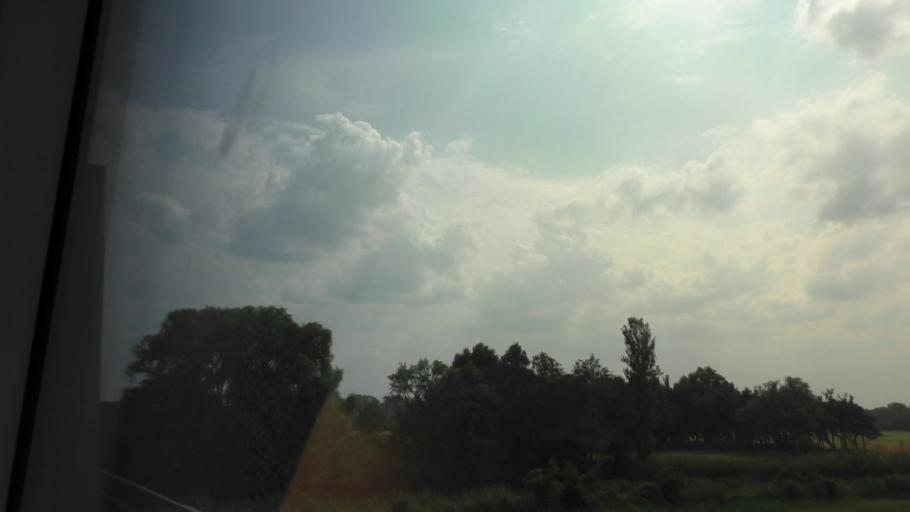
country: DE
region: Brandenburg
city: Beeskow
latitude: 52.1776
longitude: 14.2616
